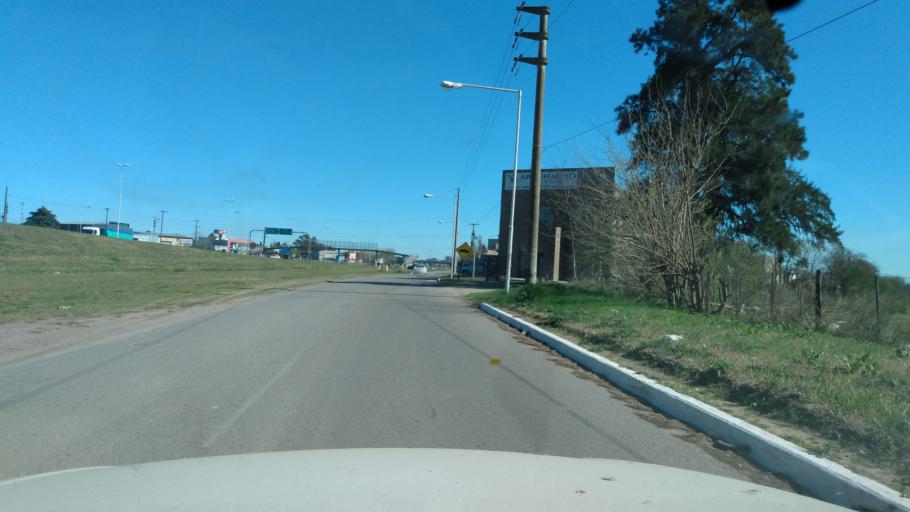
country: AR
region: Buenos Aires
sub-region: Partido de Lujan
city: Lujan
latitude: -34.5548
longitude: -59.1013
